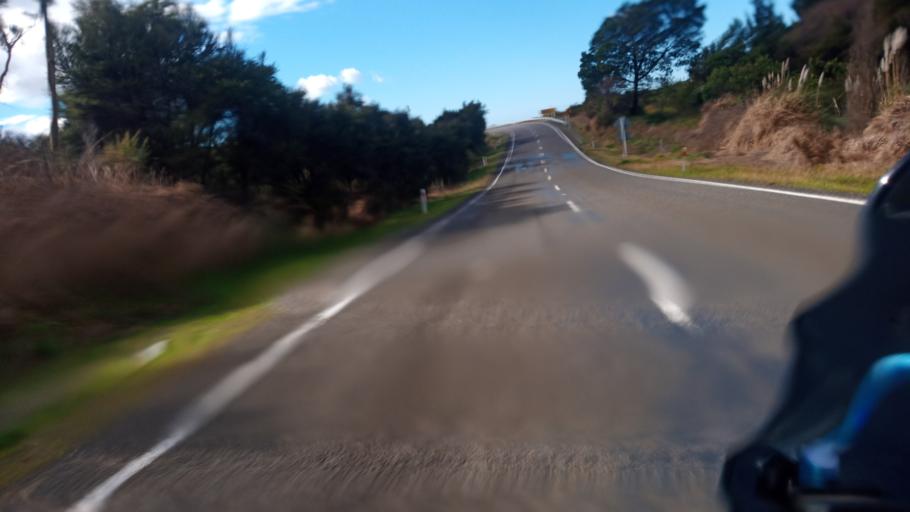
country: NZ
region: Gisborne
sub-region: Gisborne District
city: Gisborne
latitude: -37.8070
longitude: 178.3847
